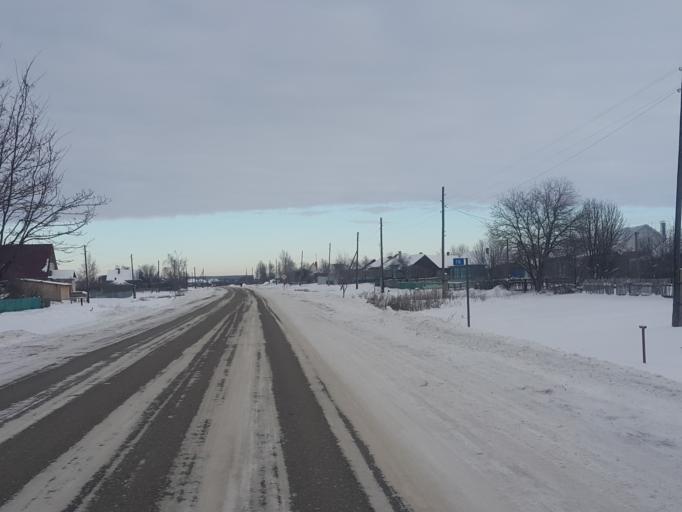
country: RU
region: Tambov
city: Platonovka
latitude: 52.8330
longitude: 41.8099
